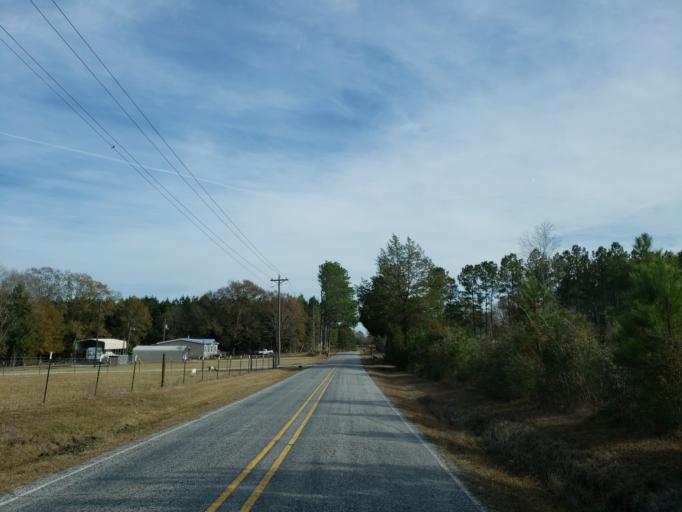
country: US
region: Mississippi
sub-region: Forrest County
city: Rawls Springs
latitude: 31.4134
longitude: -89.4139
